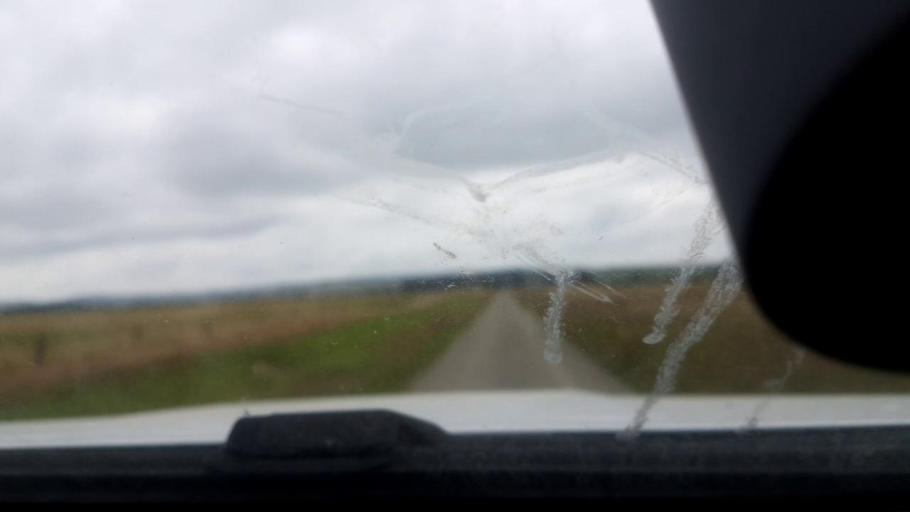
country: NZ
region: Canterbury
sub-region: Timaru District
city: Pleasant Point
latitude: -44.2306
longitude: 171.1664
